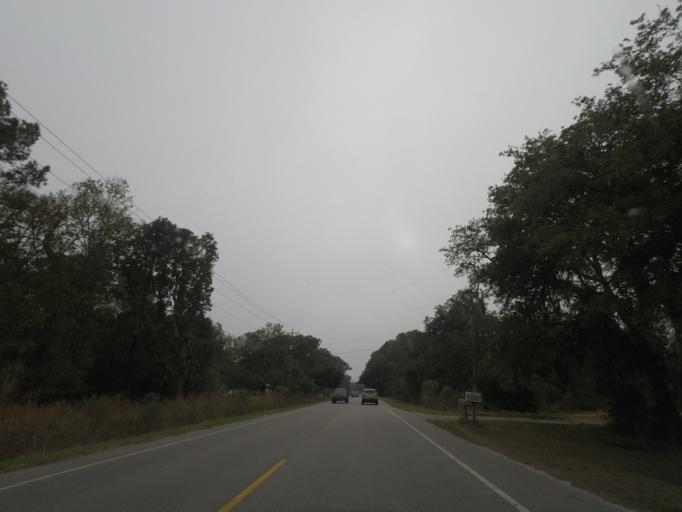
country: US
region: South Carolina
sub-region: Charleston County
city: Seabrook Island
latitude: 32.5278
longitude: -80.2967
